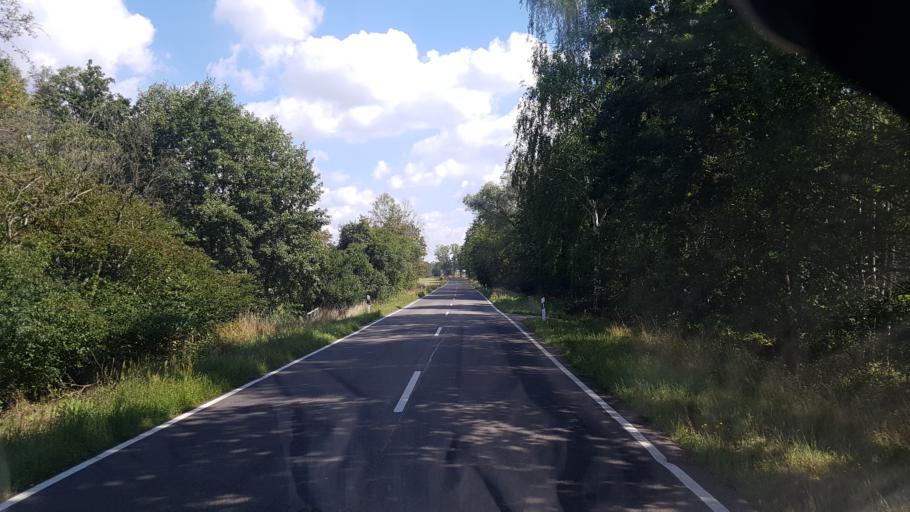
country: DE
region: Brandenburg
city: Drebkau
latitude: 51.6534
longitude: 14.3111
